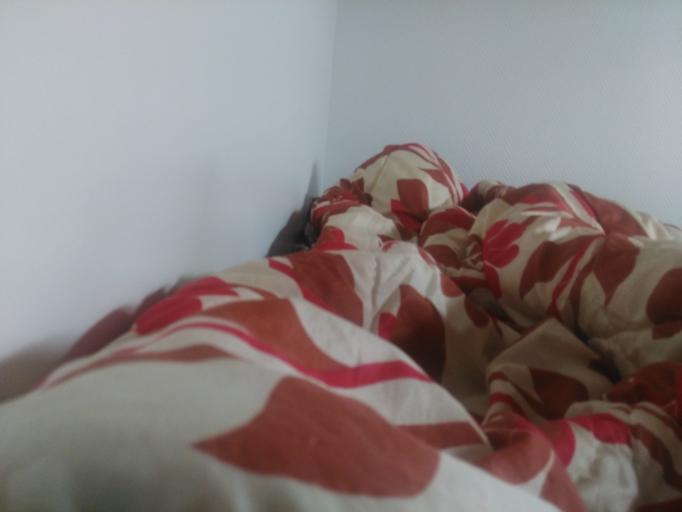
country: FR
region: Provence-Alpes-Cote d'Azur
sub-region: Departement des Alpes-Maritimes
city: Nice
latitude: 43.6935
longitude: 7.2331
